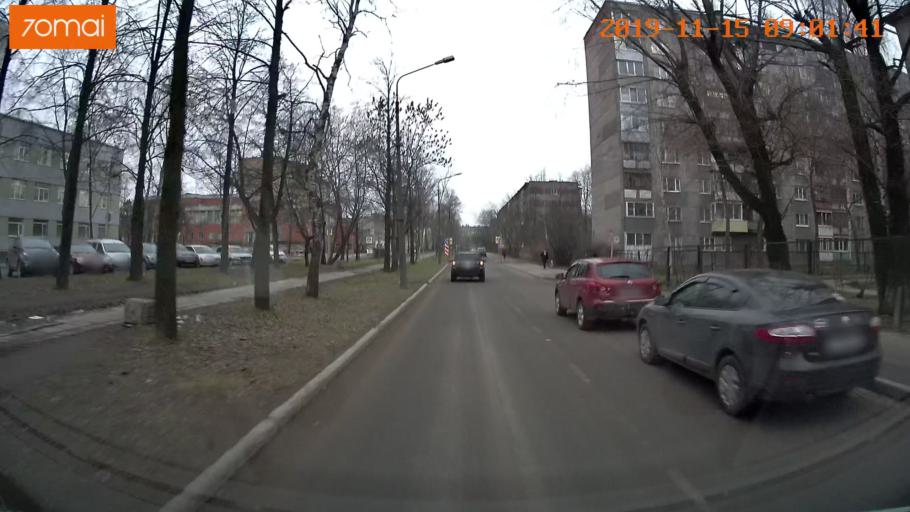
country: RU
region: Vologda
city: Cherepovets
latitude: 59.1336
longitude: 37.9264
